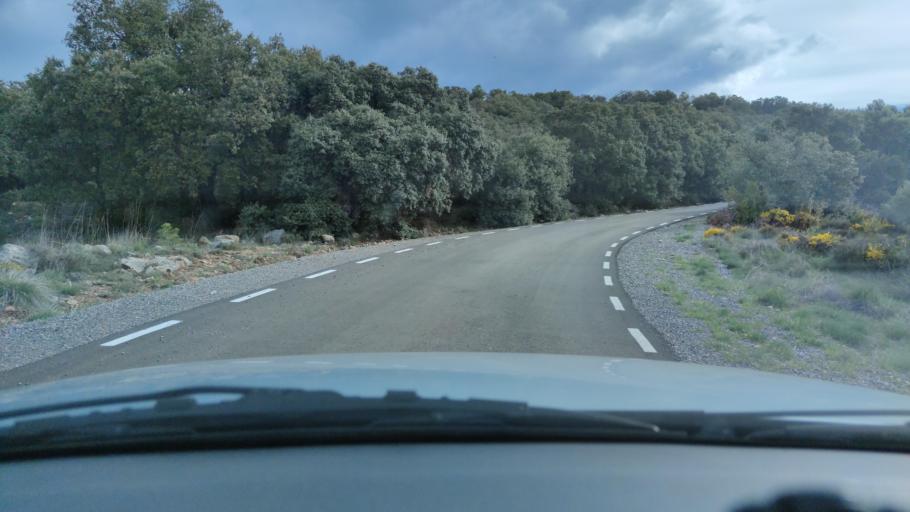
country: ES
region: Catalonia
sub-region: Provincia de Lleida
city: Coll de Nargo
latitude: 42.2408
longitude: 1.4054
